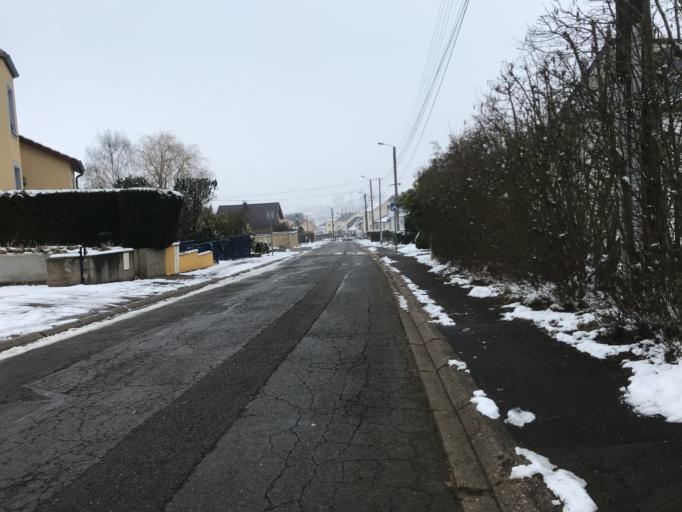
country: FR
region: Lorraine
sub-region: Departement de la Moselle
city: Russange
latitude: 49.4857
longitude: 5.9504
